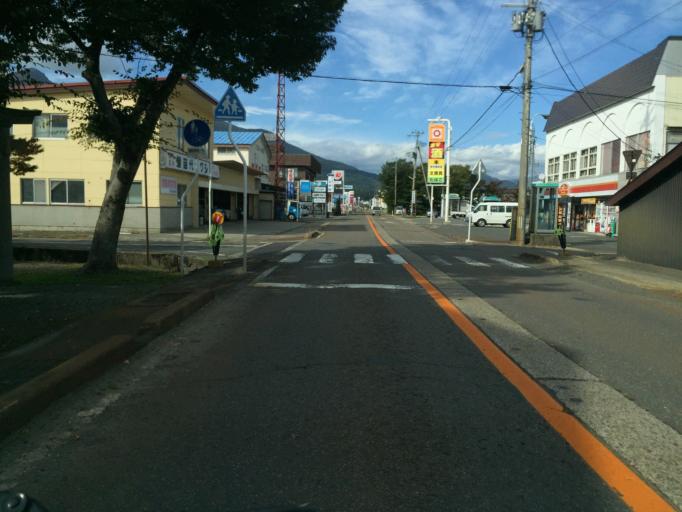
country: JP
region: Fukushima
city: Inawashiro
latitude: 37.5490
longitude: 140.1060
